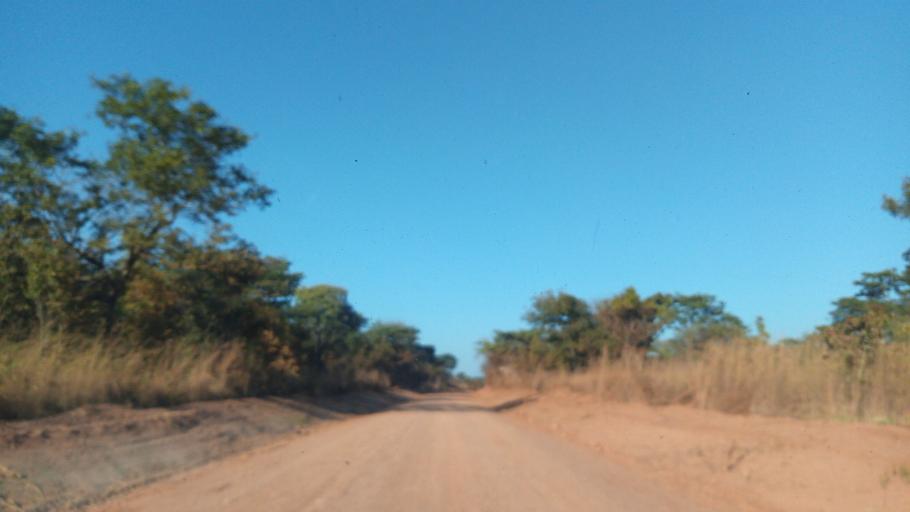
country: ZM
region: Luapula
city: Mwense
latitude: -10.4745
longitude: 28.5140
